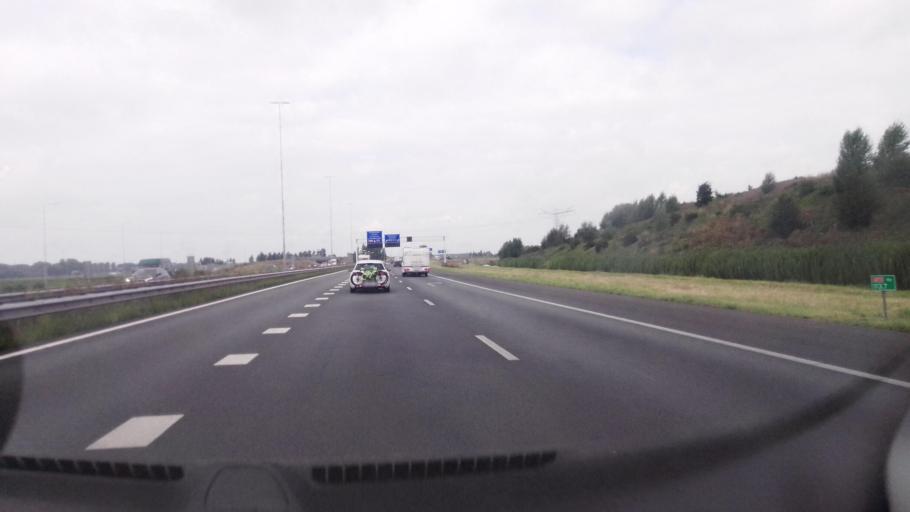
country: NL
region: Gelderland
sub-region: Gemeente Wijchen
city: Bergharen
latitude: 51.8600
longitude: 5.7165
